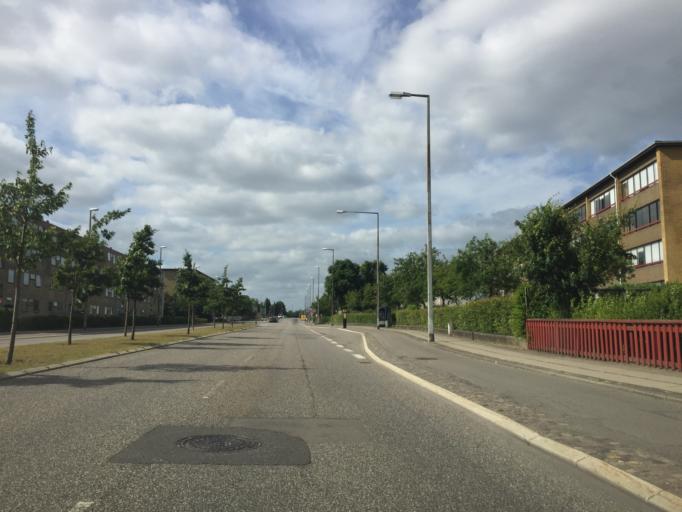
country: DK
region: Zealand
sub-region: Roskilde Kommune
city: Roskilde
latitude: 55.6284
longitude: 12.0909
